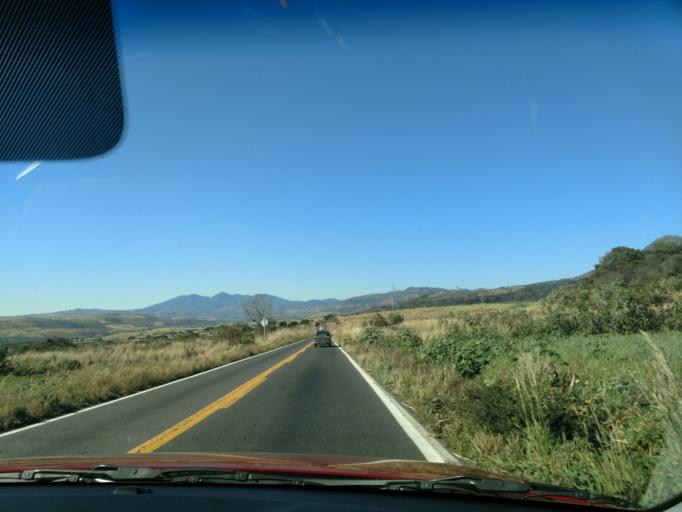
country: MX
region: Nayarit
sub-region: Ahuacatlan
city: Ahuacatlan
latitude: 21.1150
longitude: -104.5903
